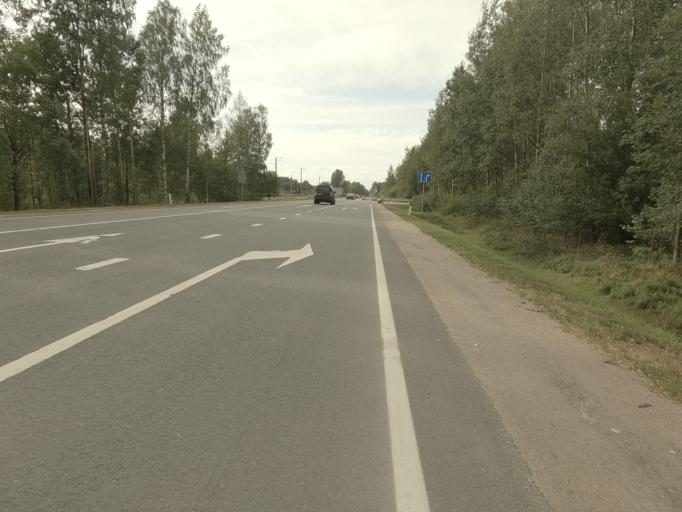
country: RU
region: Leningrad
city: Kirovsk
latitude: 59.8537
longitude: 31.0194
